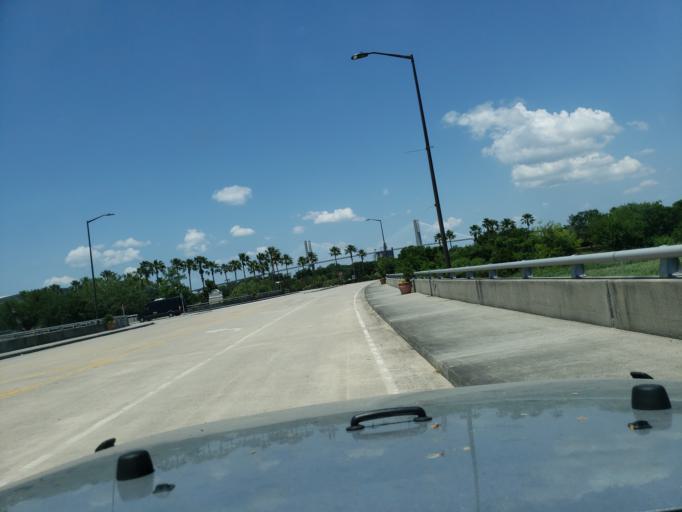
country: US
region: Georgia
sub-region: Chatham County
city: Savannah
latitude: 32.0856
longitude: -81.0838
